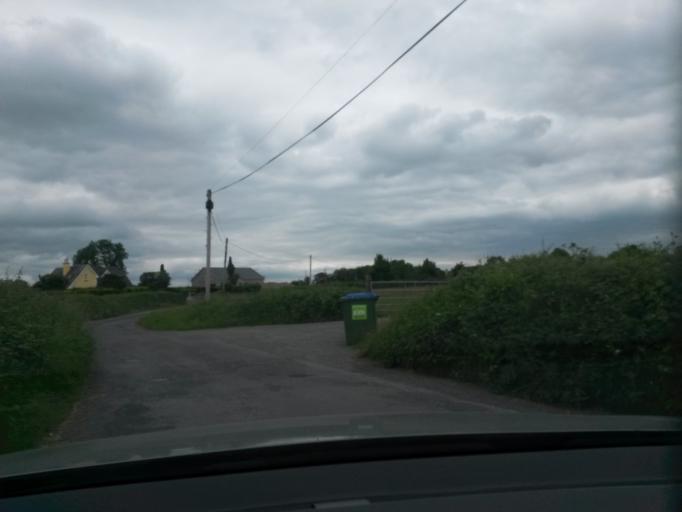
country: IE
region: Munster
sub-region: An Clar
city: Ennis
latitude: 52.9131
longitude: -9.0542
